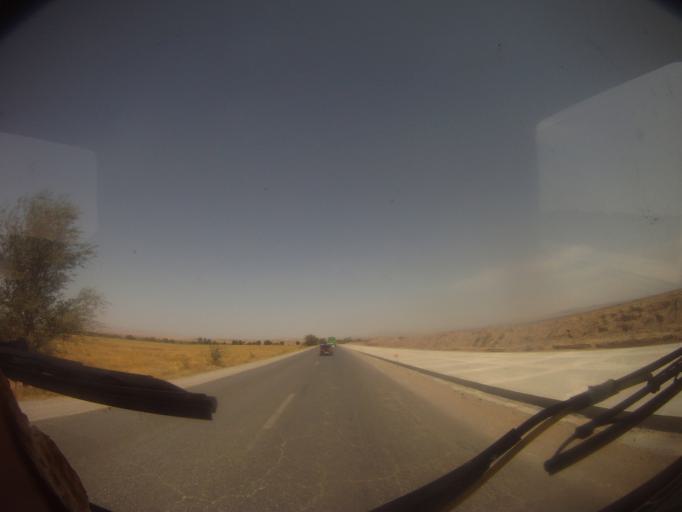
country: KZ
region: Ongtustik Qazaqstan
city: Aksu
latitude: 42.4672
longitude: 69.7898
